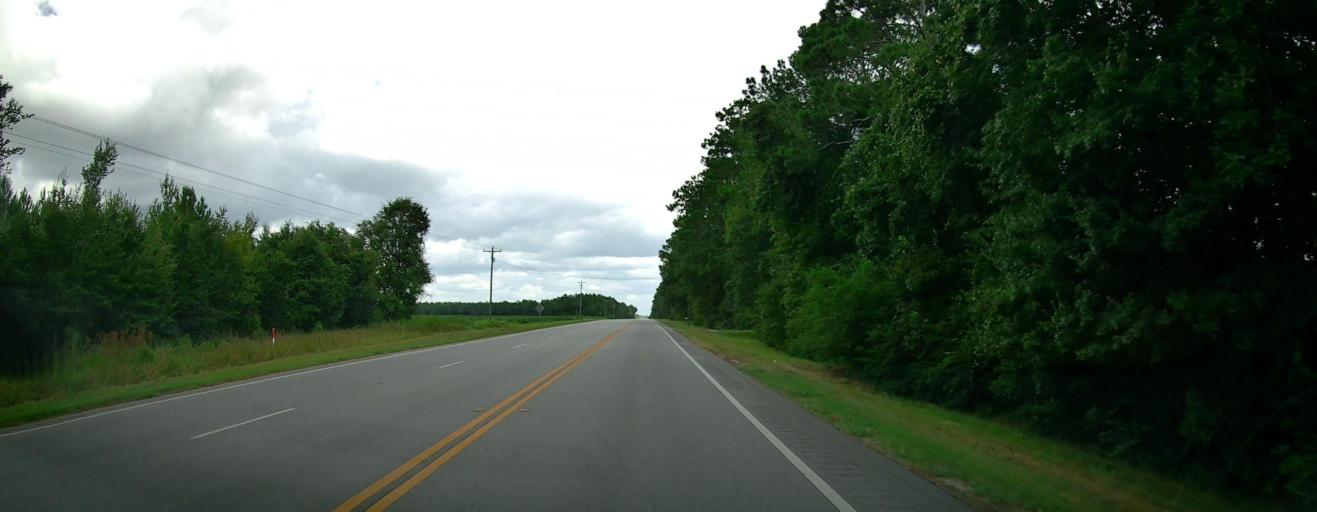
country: US
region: Georgia
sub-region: Coffee County
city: Broxton
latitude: 31.5701
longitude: -83.0212
